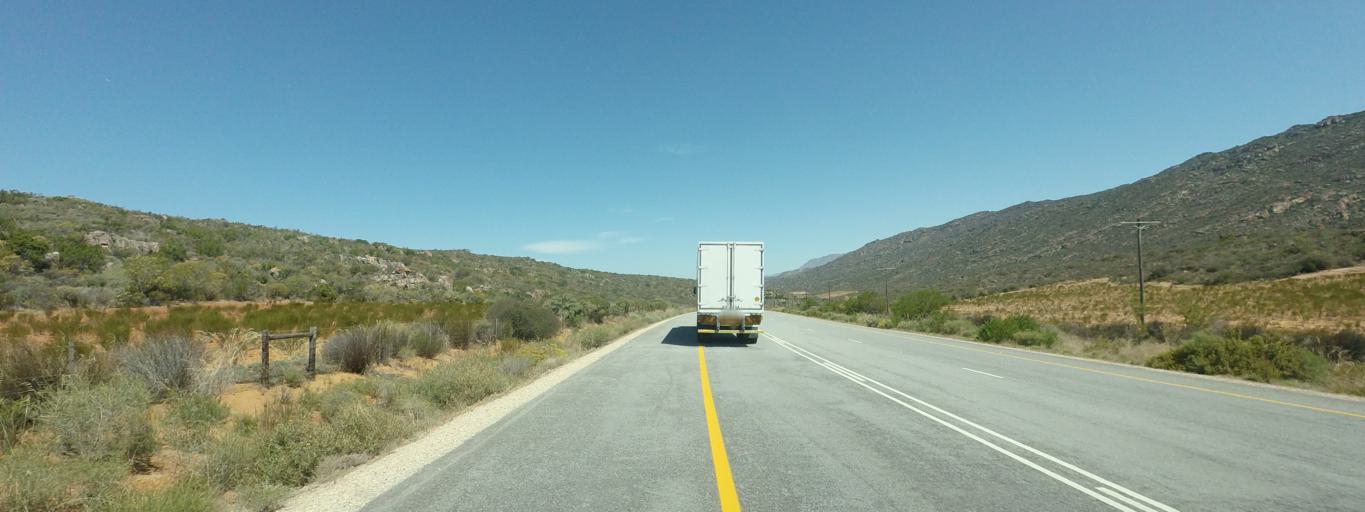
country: ZA
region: Western Cape
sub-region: West Coast District Municipality
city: Clanwilliam
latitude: -32.3308
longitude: 18.9242
